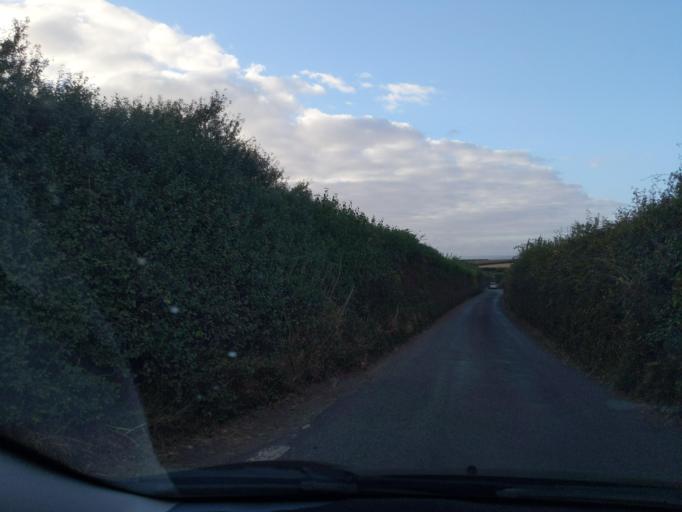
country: GB
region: England
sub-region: Devon
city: Salcombe
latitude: 50.2360
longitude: -3.8201
